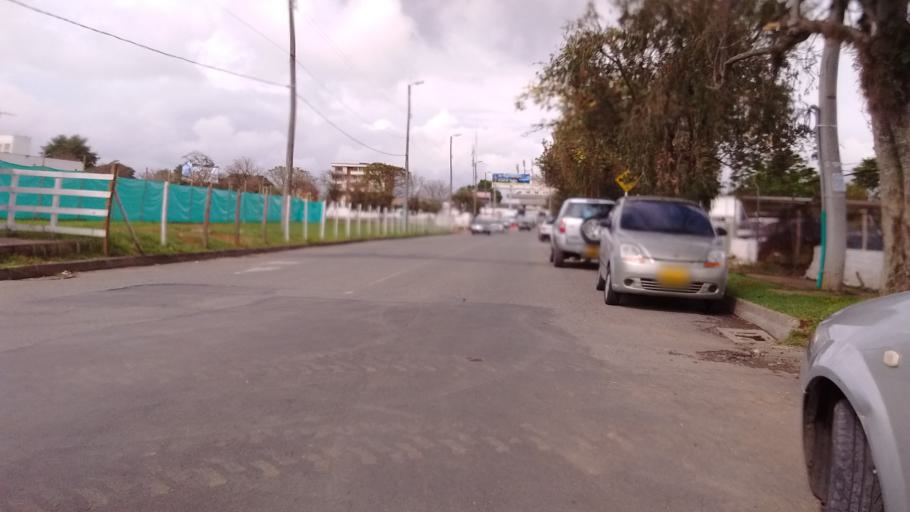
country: CO
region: Cauca
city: Popayan
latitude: 2.4552
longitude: -76.6004
